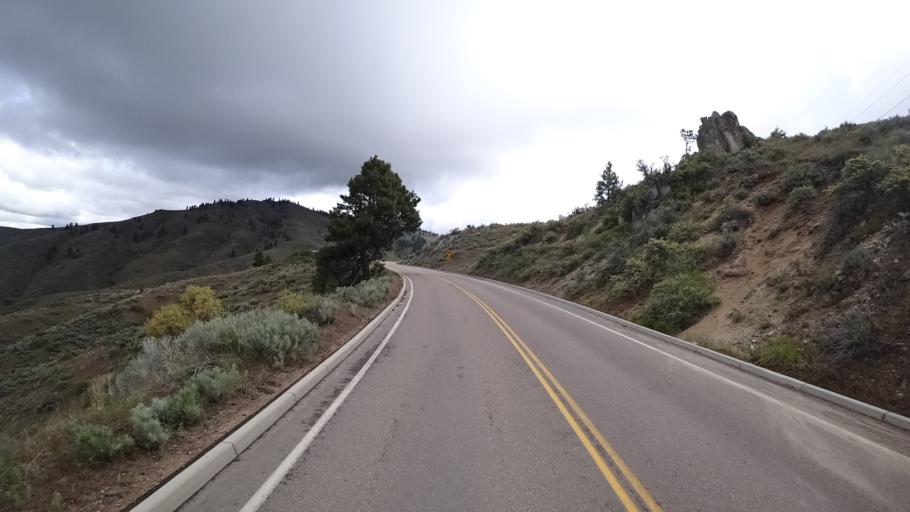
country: US
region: Idaho
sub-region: Ada County
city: Boise
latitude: 43.7249
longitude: -116.1578
